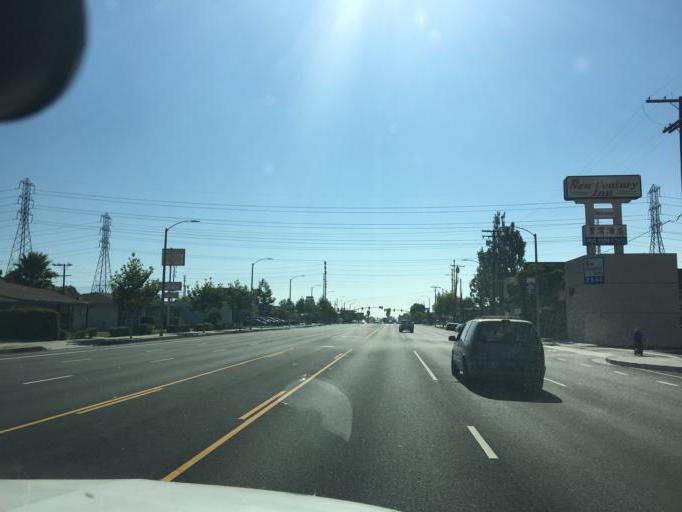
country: US
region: California
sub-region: Los Angeles County
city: East San Gabriel
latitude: 34.1035
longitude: -118.0844
